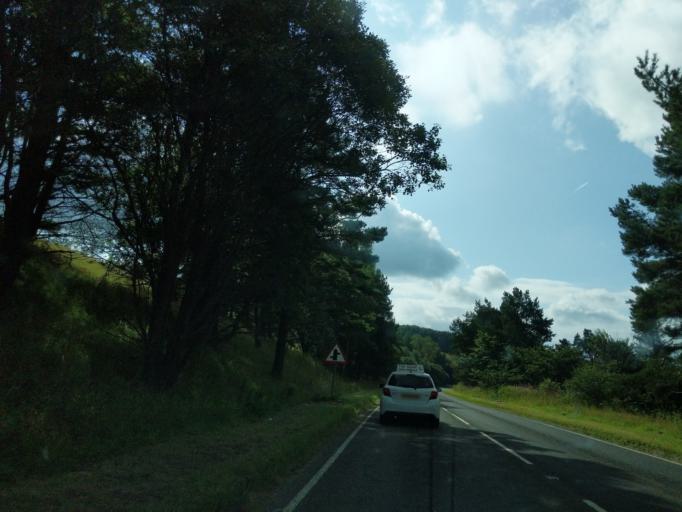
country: GB
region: Scotland
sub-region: Midlothian
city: Penicuik
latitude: 55.7492
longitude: -3.2056
